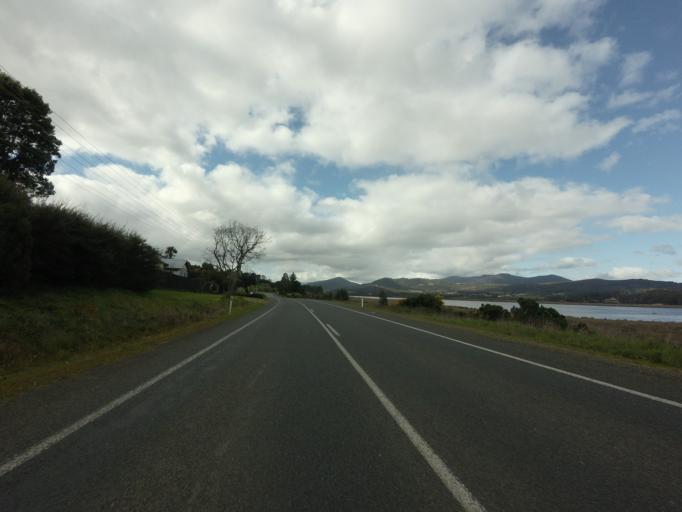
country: AU
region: Tasmania
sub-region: Huon Valley
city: Franklin
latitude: -43.1168
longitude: 146.9924
